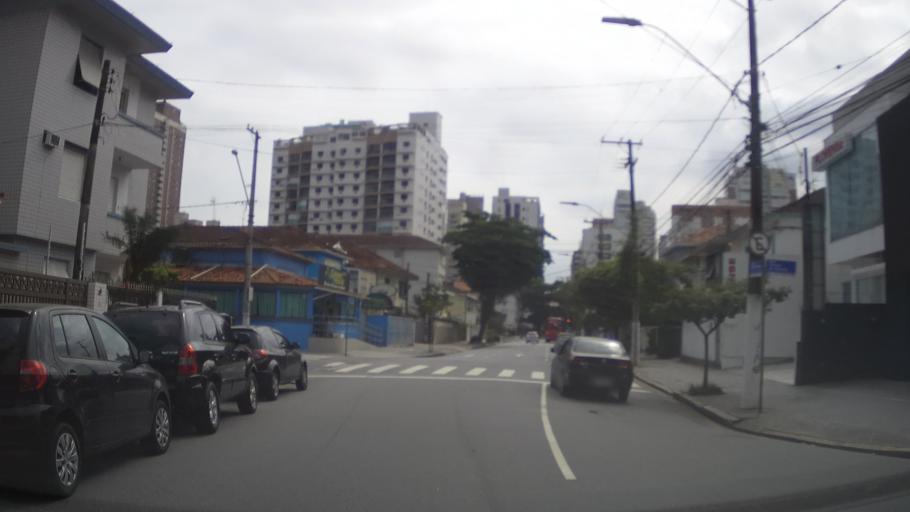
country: BR
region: Sao Paulo
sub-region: Santos
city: Santos
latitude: -23.9668
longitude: -46.3207
